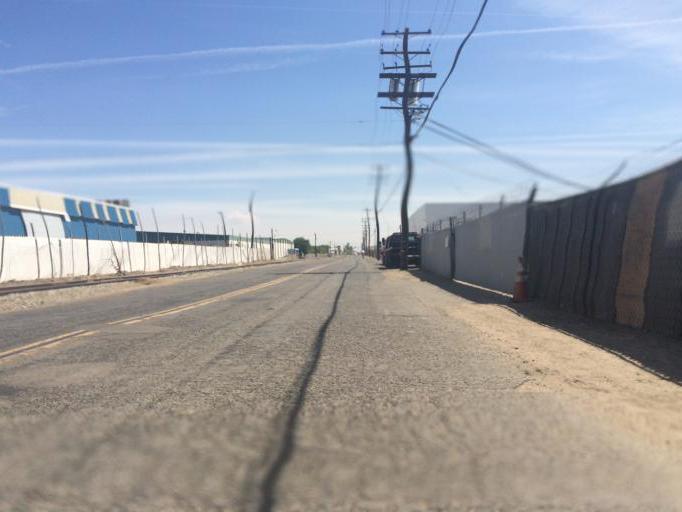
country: US
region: California
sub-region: Fresno County
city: Fresno
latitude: 36.7214
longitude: -119.7772
